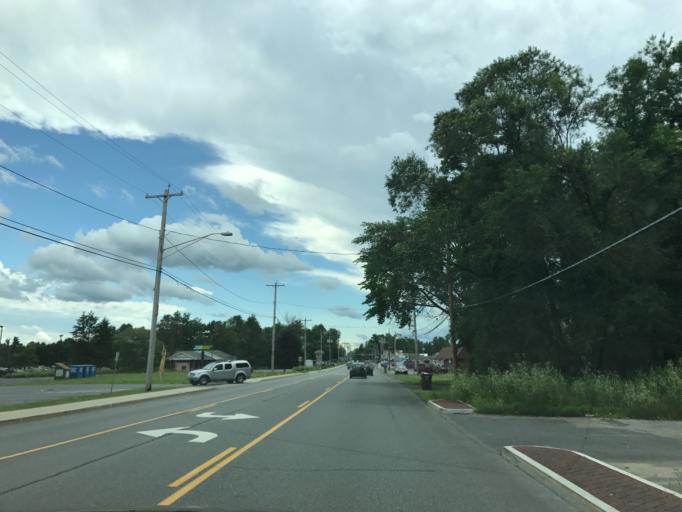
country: US
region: New York
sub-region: Saratoga County
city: South Glens Falls
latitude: 43.2882
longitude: -73.6391
